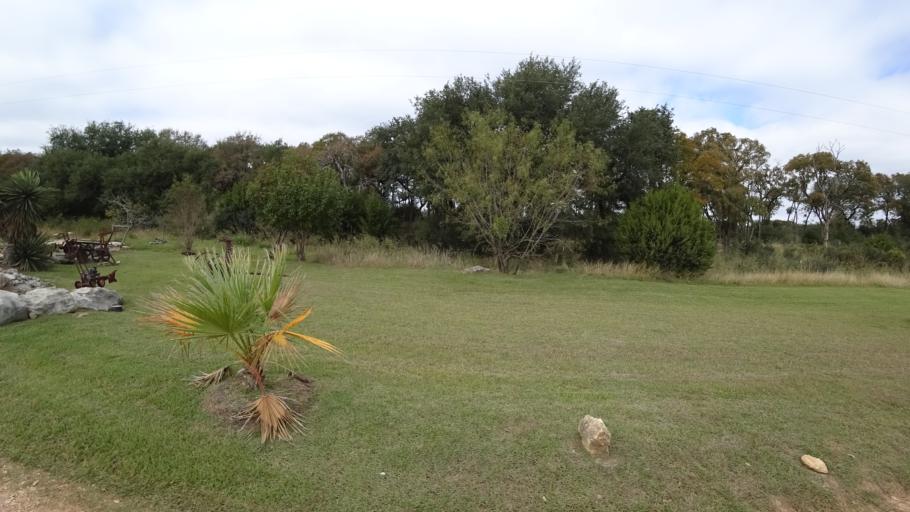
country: US
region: Texas
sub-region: Travis County
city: Shady Hollow
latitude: 30.1291
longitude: -97.8840
